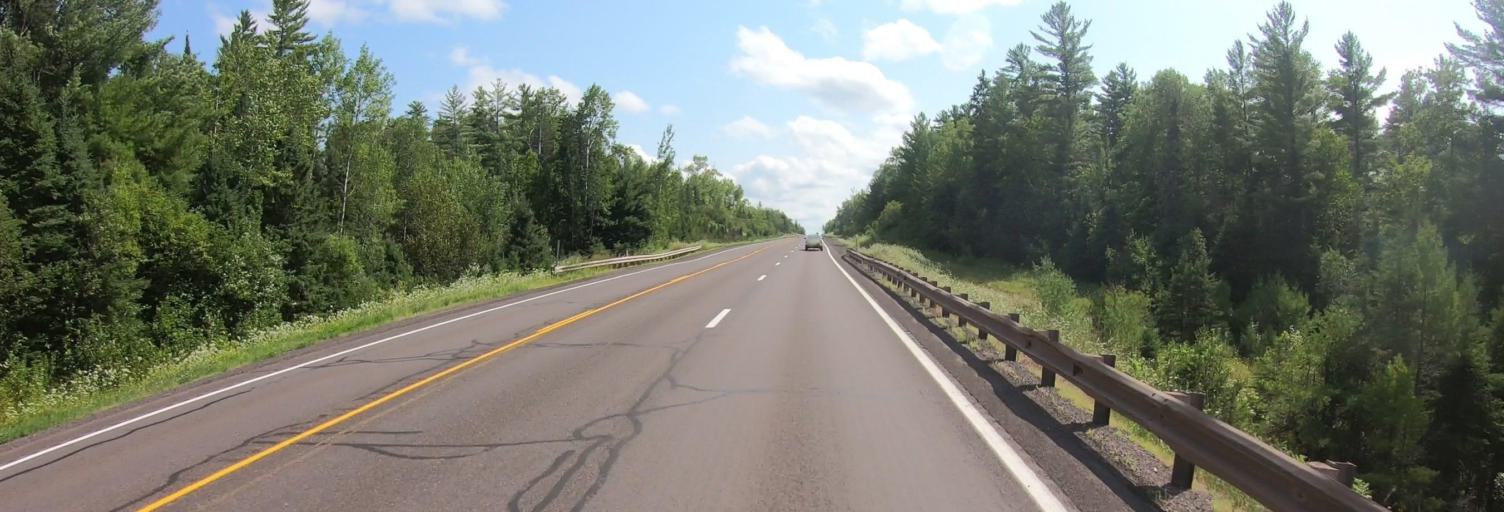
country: US
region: Michigan
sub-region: Ontonagon County
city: Ontonagon
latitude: 46.6804
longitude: -89.1661
